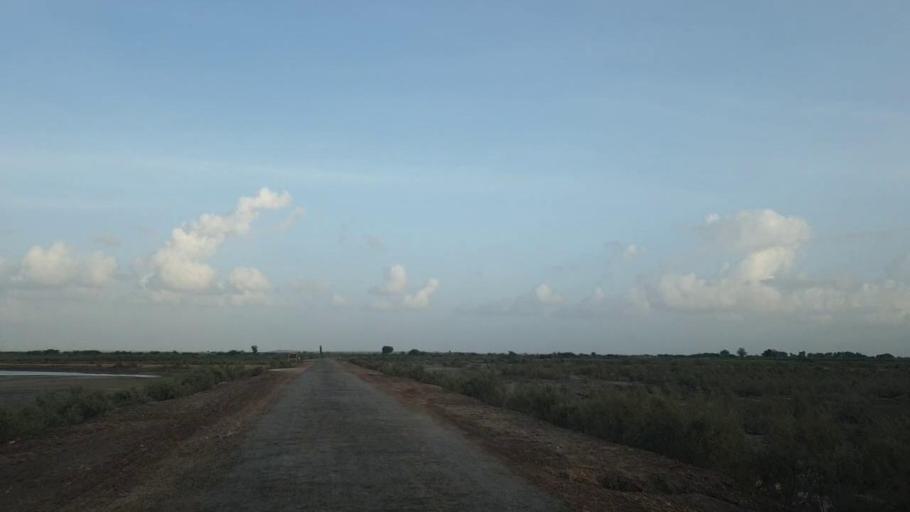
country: PK
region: Sindh
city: Kadhan
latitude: 24.5655
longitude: 69.1204
